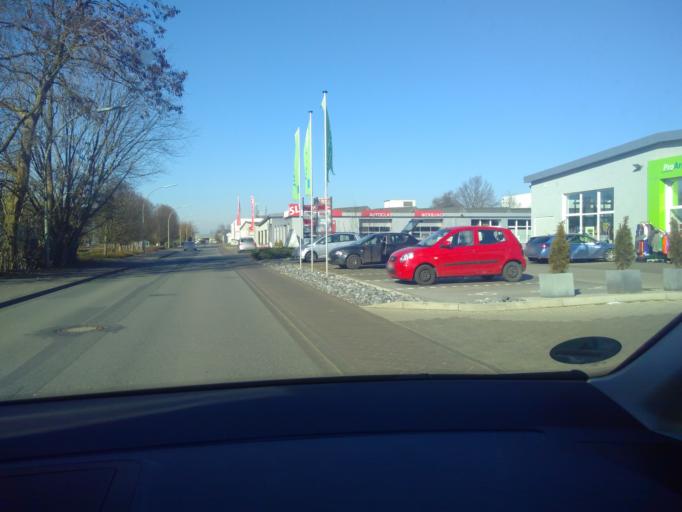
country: DE
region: North Rhine-Westphalia
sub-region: Regierungsbezirk Detmold
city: Rheda-Wiedenbruck
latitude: 51.8395
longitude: 8.2952
